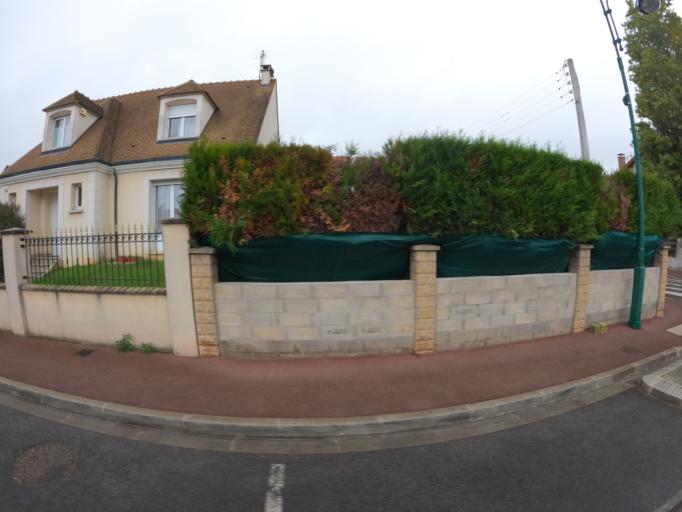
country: FR
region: Ile-de-France
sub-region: Departement du Val-de-Marne
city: Ormesson-sur-Marne
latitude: 48.7880
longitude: 2.5343
